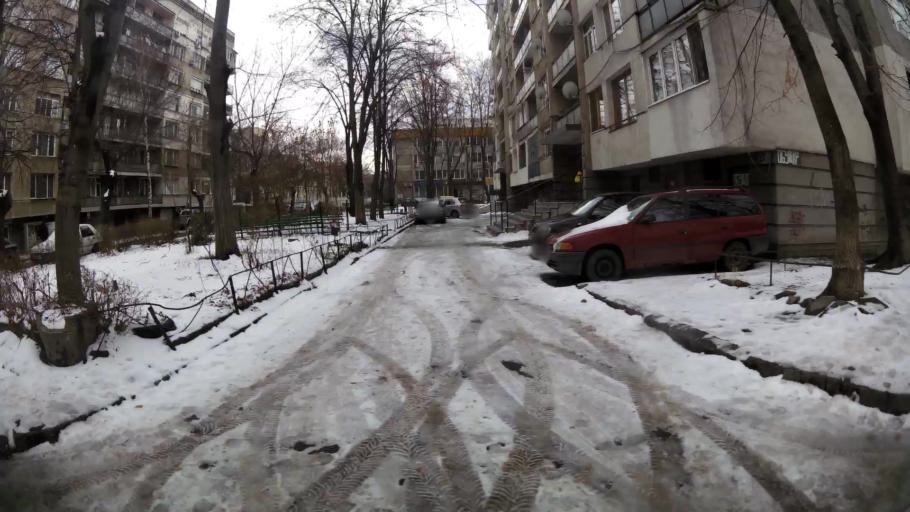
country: BG
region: Sofia-Capital
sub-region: Stolichna Obshtina
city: Sofia
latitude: 42.7019
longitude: 23.3616
